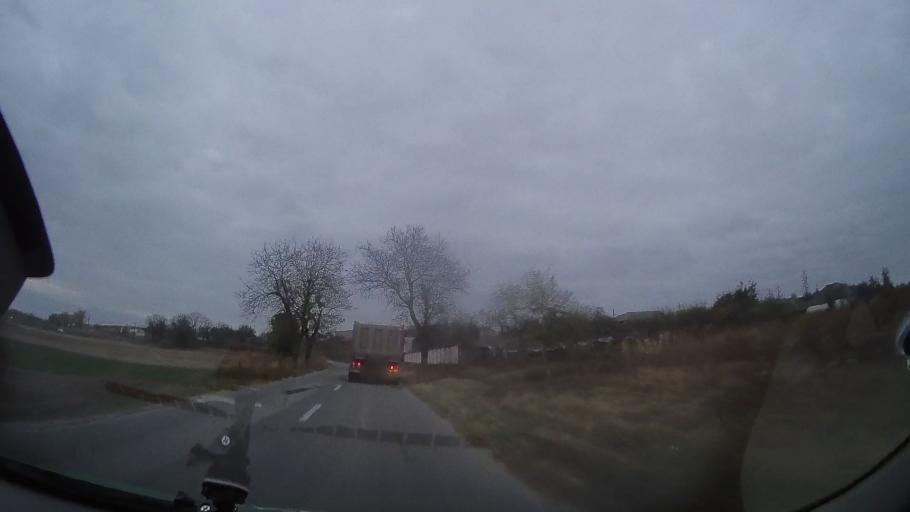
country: RO
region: Tulcea
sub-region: Comuna Mihai Bravu
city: Mihai Bravu
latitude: 44.9549
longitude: 28.6527
